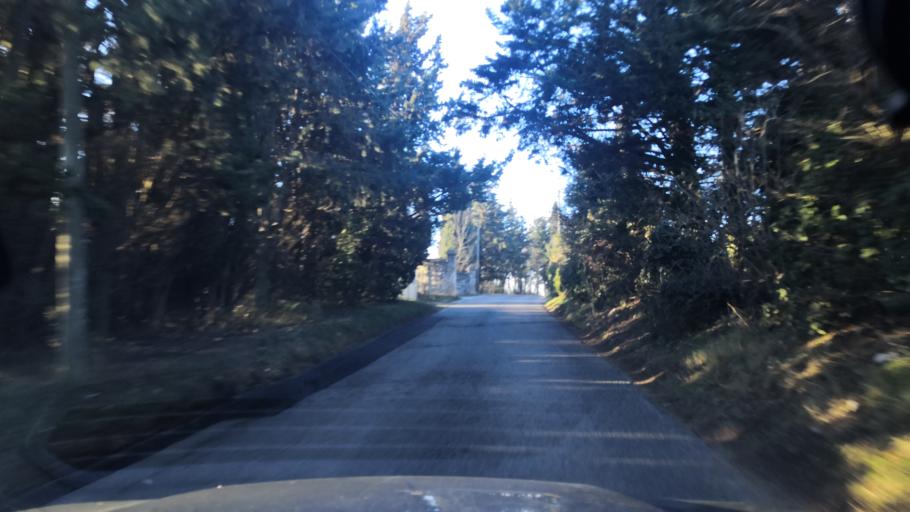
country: FR
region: Provence-Alpes-Cote d'Azur
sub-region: Departement des Bouches-du-Rhone
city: Aix-en-Provence
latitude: 43.5178
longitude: 5.4156
